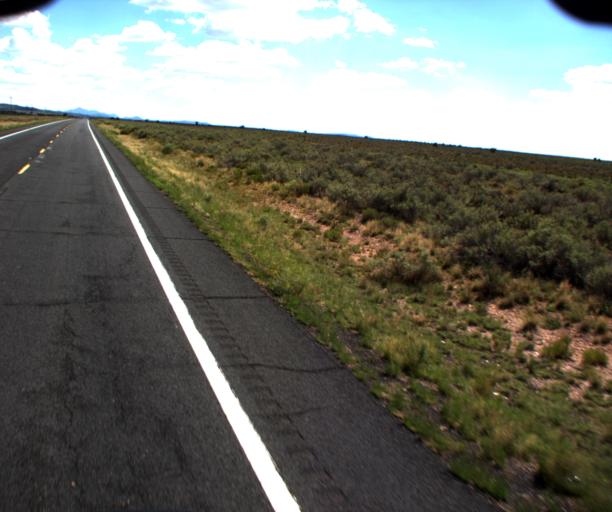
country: US
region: Arizona
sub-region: Coconino County
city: Williams
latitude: 35.6133
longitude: -112.1448
